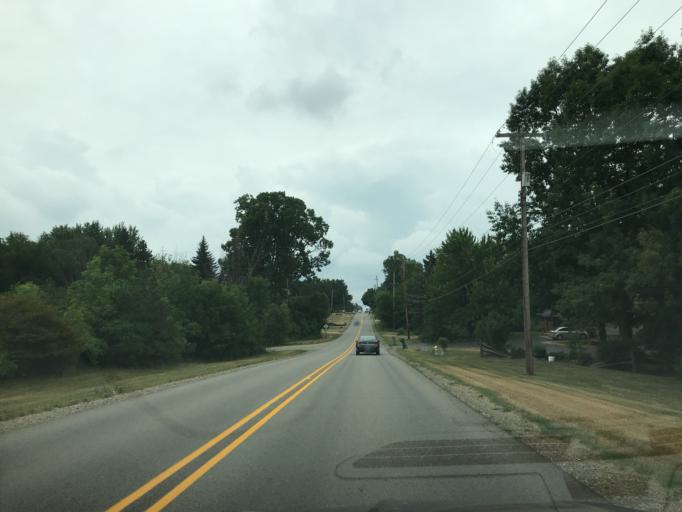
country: US
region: Michigan
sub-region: Eaton County
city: Waverly
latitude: 42.7176
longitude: -84.6621
